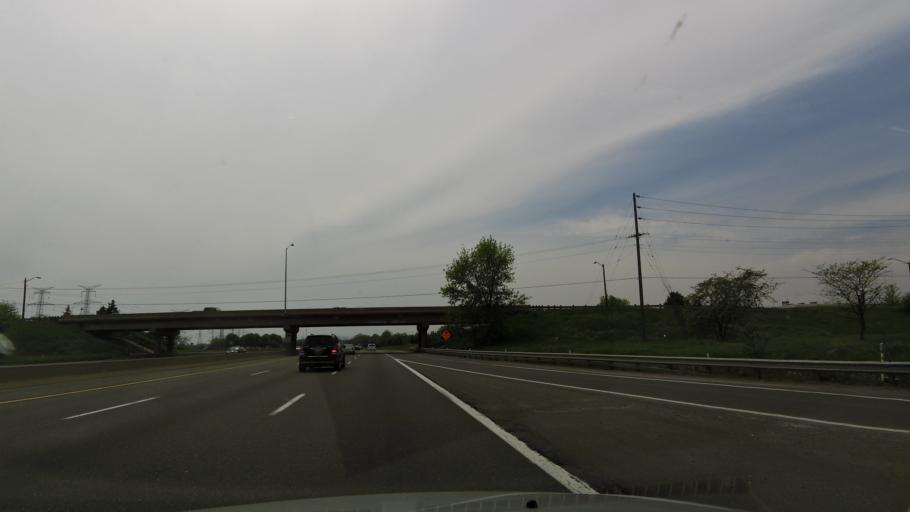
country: CA
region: Ontario
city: Oshawa
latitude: 43.8951
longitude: -78.6885
